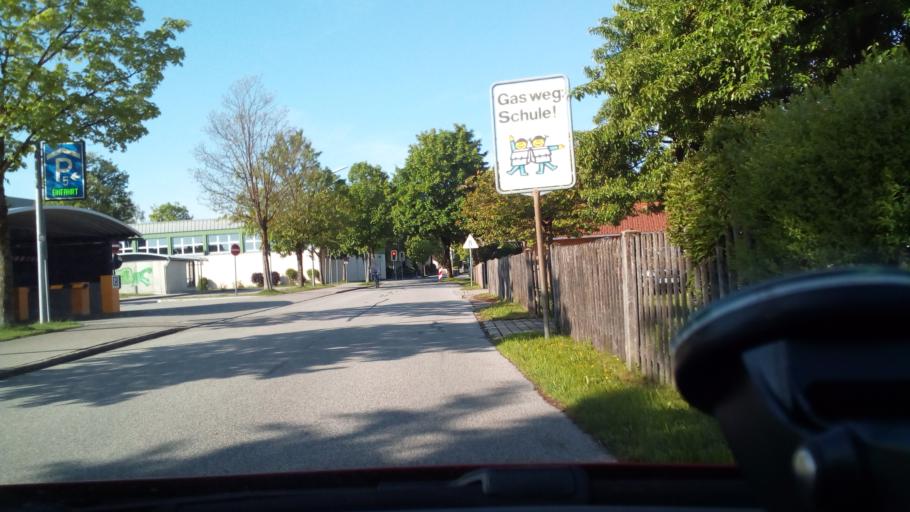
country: DE
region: Bavaria
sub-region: Upper Bavaria
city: Holzkirchen
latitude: 47.8772
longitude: 11.6980
